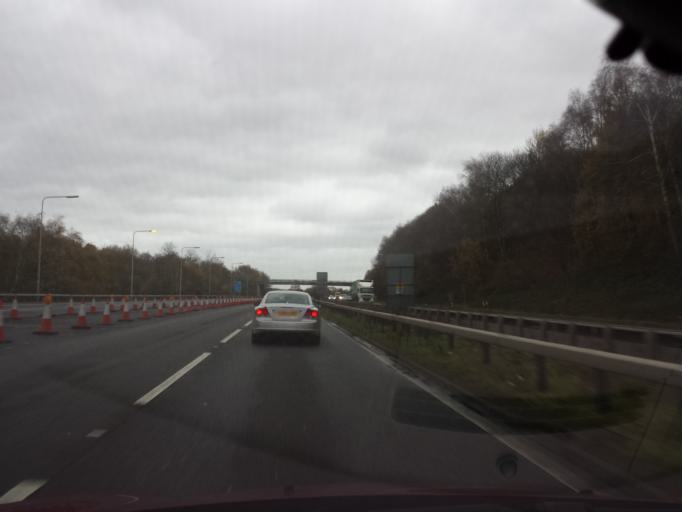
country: GB
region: England
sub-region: Surrey
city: Chertsey
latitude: 51.4011
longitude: -0.5295
